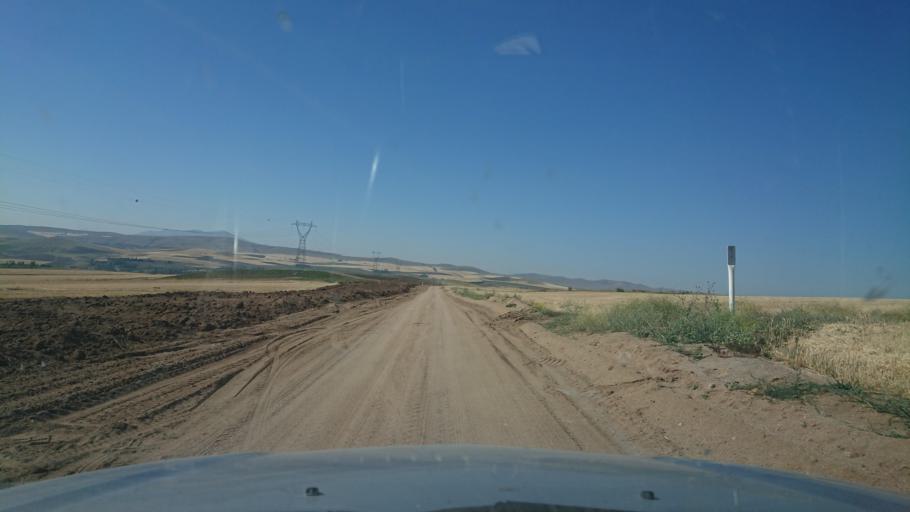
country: TR
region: Aksaray
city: Agacoren
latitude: 38.8398
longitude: 33.9442
